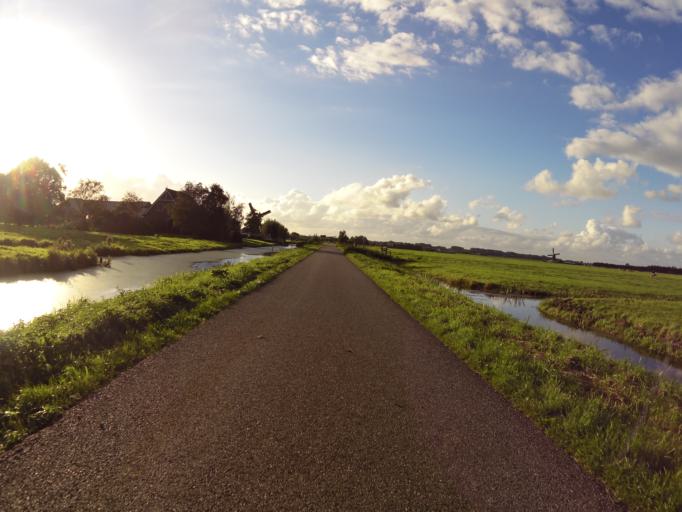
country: NL
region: South Holland
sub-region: Bodegraven-Reeuwijk
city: Bodegraven
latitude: 52.1280
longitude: 4.7297
